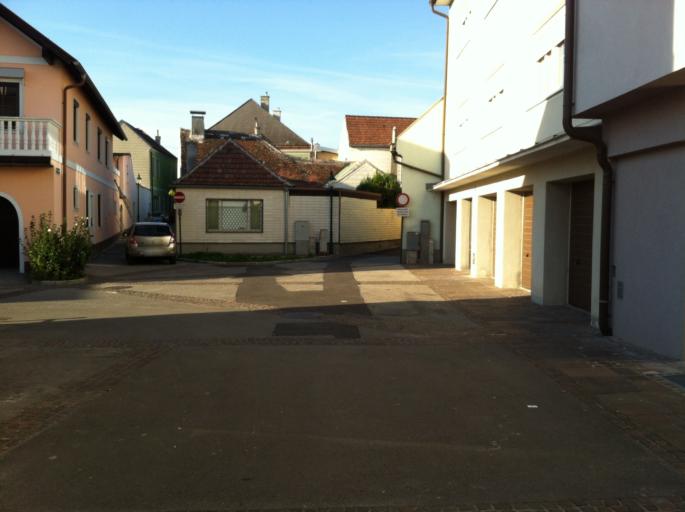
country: AT
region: Lower Austria
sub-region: Politischer Bezirk Tulln
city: Tulln
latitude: 48.3318
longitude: 16.0527
